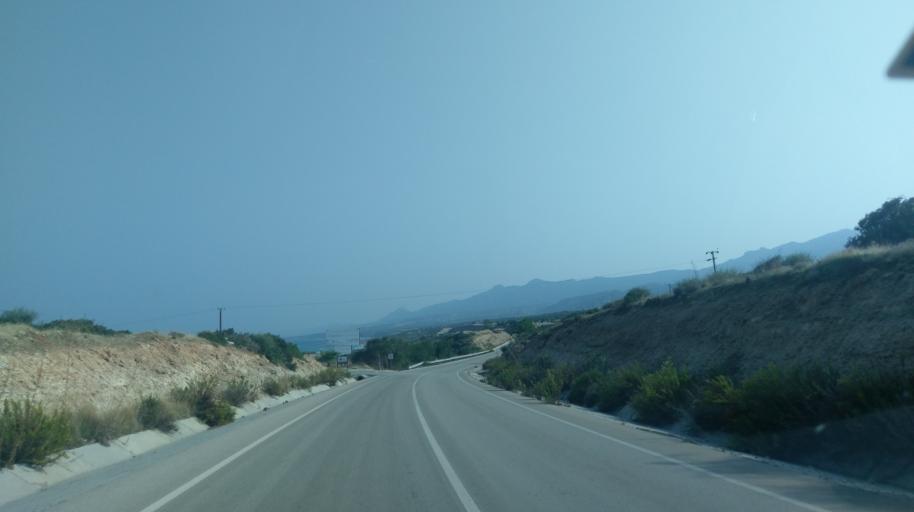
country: CY
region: Ammochostos
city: Trikomo
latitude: 35.4101
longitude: 33.8182
